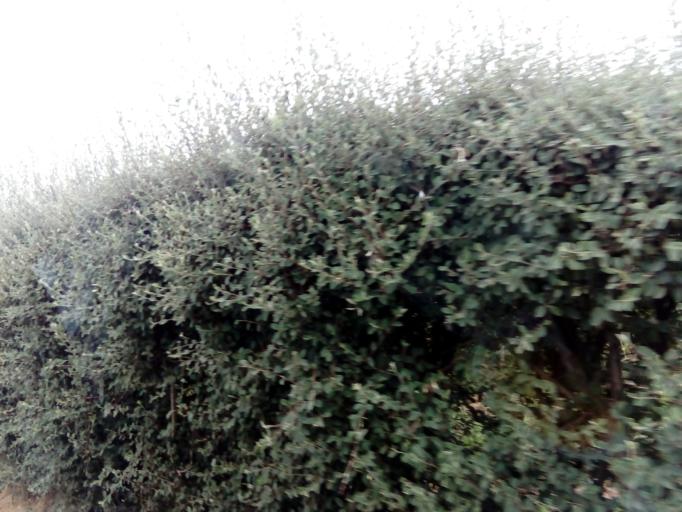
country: LS
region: Berea
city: Teyateyaneng
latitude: -29.1165
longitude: 27.9622
